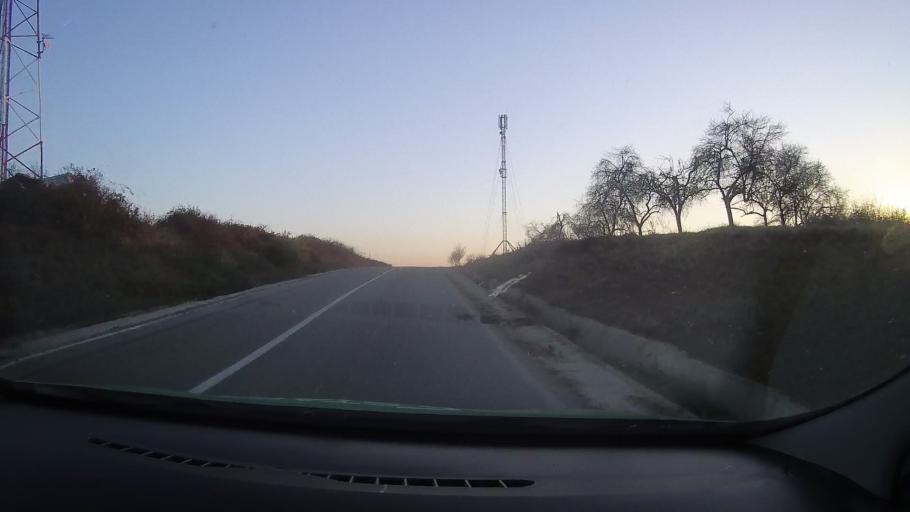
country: RO
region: Timis
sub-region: Comuna Manastiur
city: Manastiur
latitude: 45.8245
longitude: 22.0715
